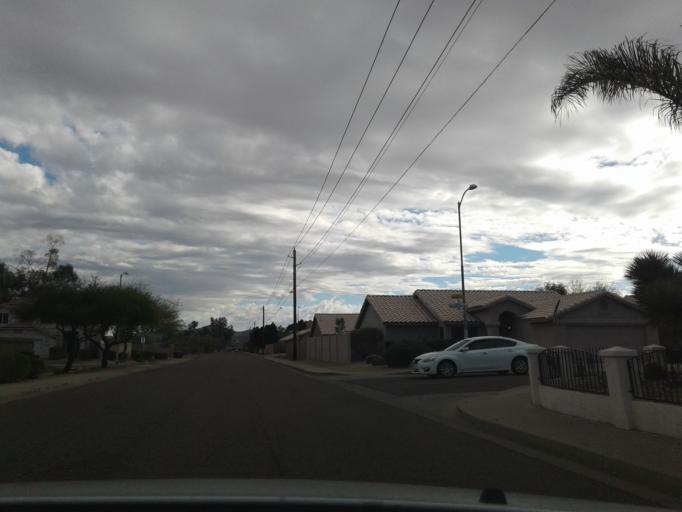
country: US
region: Arizona
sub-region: Maricopa County
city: Glendale
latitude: 33.6524
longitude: -112.0893
